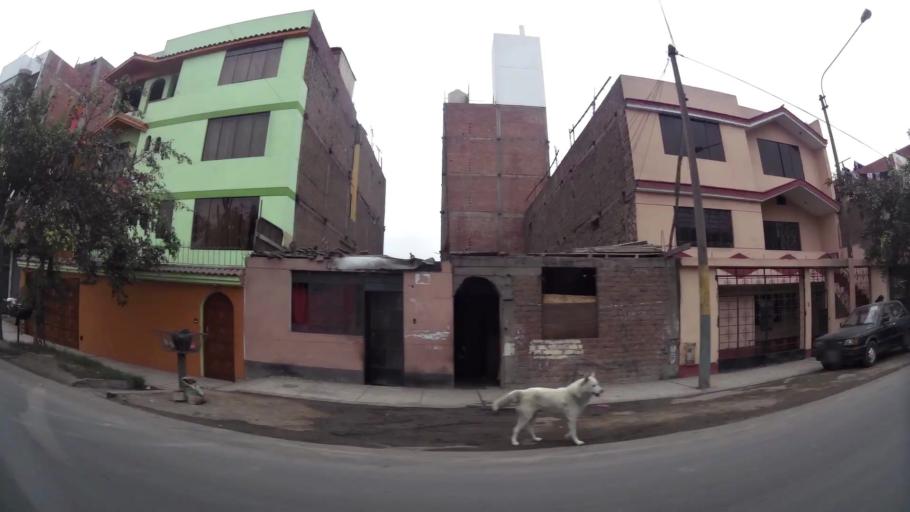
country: PE
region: Lima
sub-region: Lima
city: Vitarte
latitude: -12.0429
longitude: -76.9678
